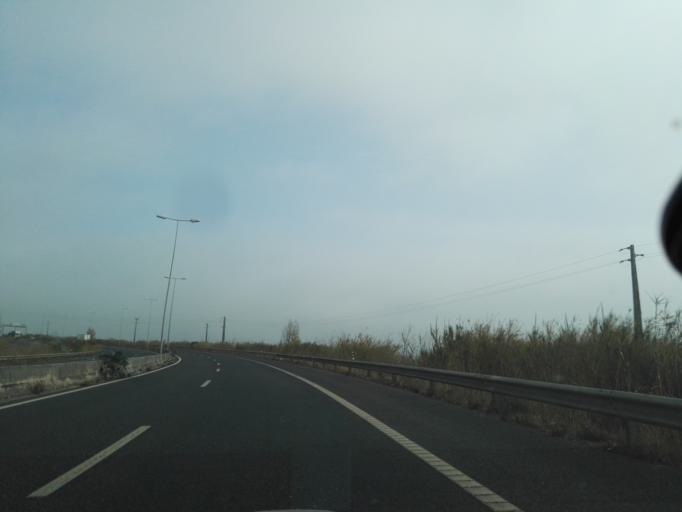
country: PT
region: Lisbon
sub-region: Loures
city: Bobadela
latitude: 38.8002
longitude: -9.0934
